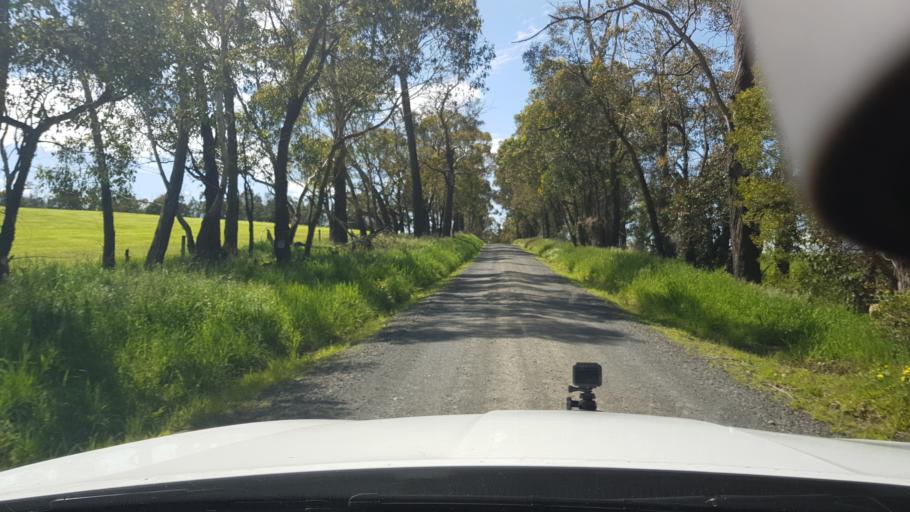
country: AU
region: Victoria
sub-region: Latrobe
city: Moe
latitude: -38.1493
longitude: 146.1309
